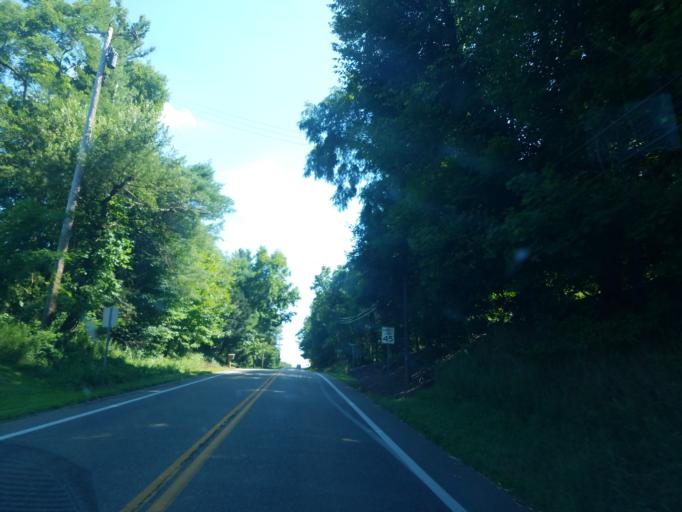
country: US
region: Ohio
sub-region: Portage County
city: Ravenna
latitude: 41.1844
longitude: -81.2465
